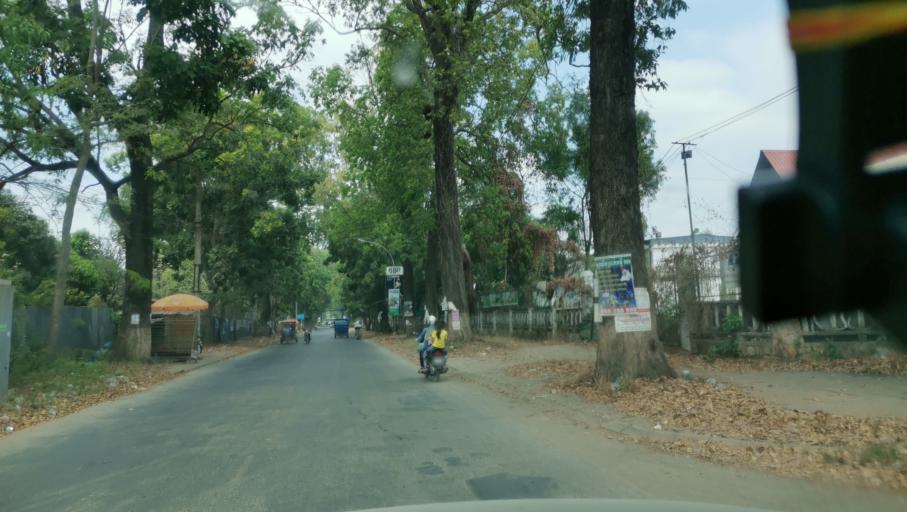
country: KH
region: Battambang
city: Battambang
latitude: 13.0882
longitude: 103.2002
